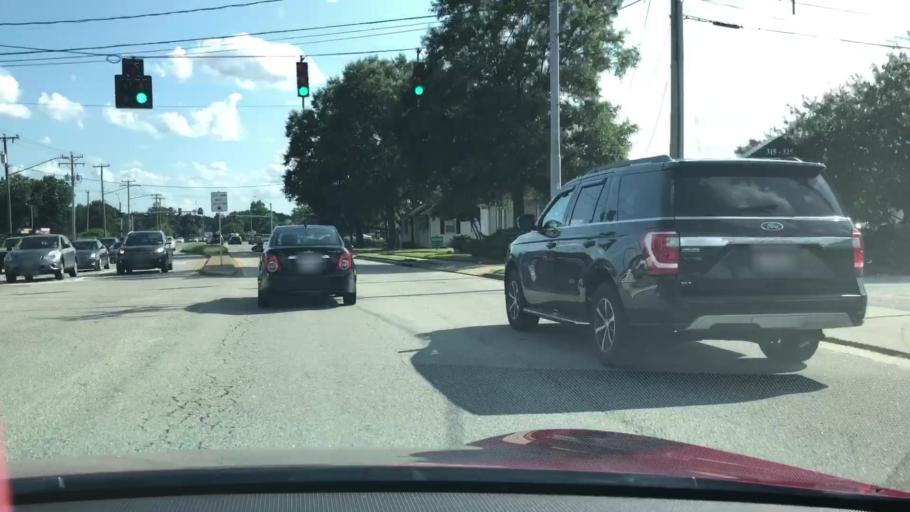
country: US
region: Virginia
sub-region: City of Virginia Beach
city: Virginia Beach
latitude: 36.8442
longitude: -76.0209
